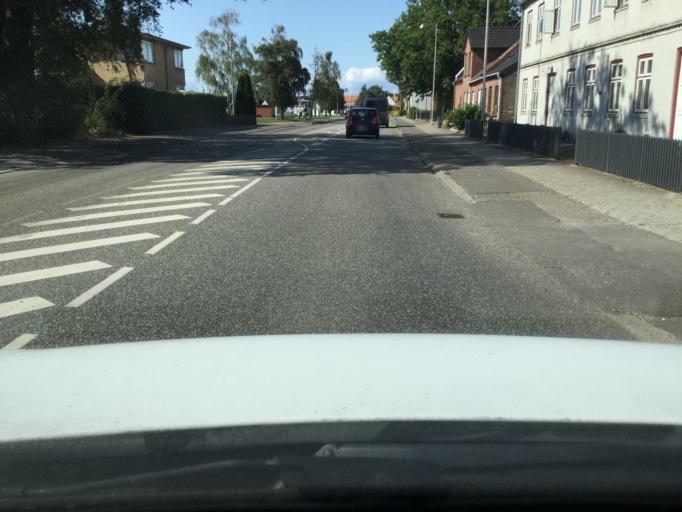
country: DK
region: Zealand
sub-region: Lolland Kommune
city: Nakskov
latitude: 54.8264
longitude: 11.1474
